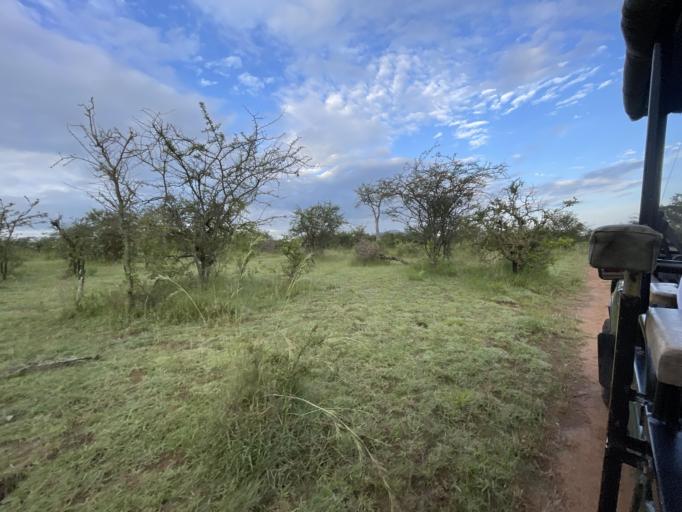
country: TZ
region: Mara
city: Mugumu
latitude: -1.7029
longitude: 35.3083
